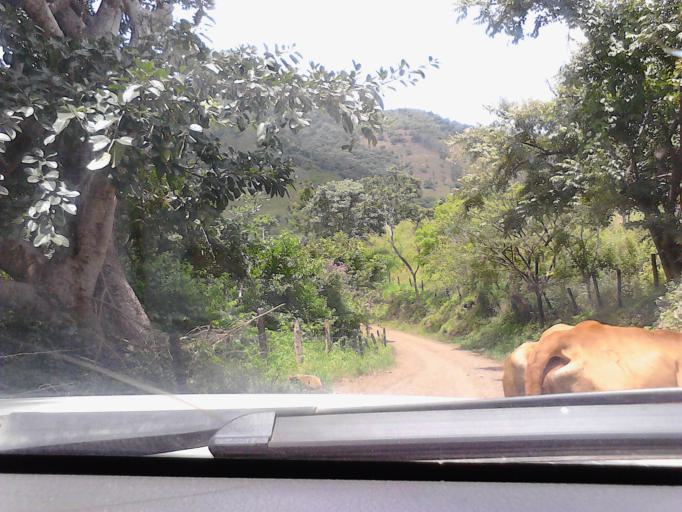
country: NI
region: Matagalpa
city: Terrabona
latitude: 12.7122
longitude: -85.9419
